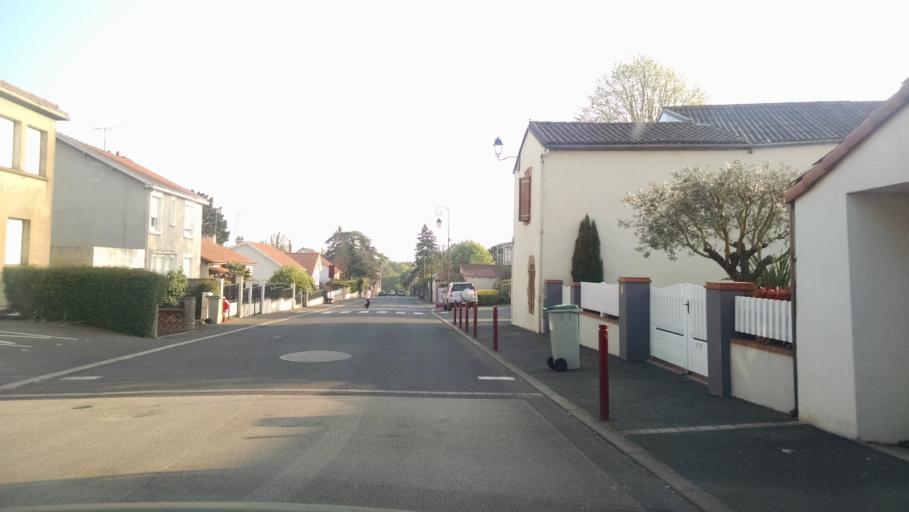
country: FR
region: Pays de la Loire
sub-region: Departement de la Loire-Atlantique
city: Boussay
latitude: 47.0427
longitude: -1.1875
